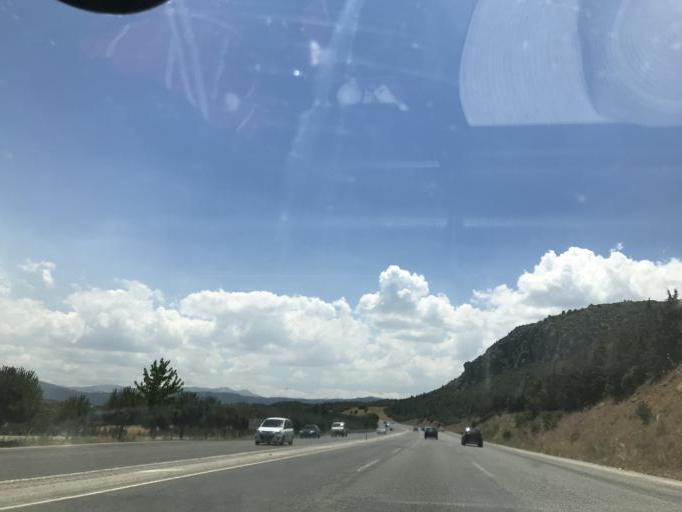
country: TR
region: Denizli
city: Honaz
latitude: 37.7143
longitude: 29.2066
